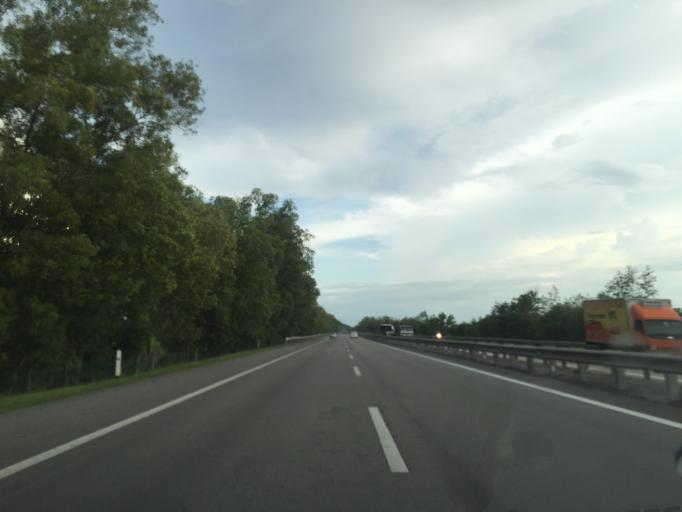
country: MY
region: Kedah
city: Gurun
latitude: 5.9596
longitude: 100.4483
